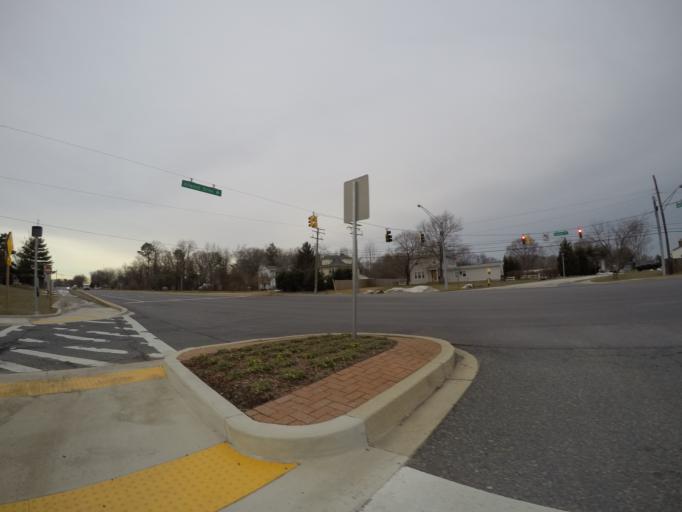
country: US
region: Maryland
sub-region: Anne Arundel County
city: Ferndale
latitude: 39.1798
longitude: -76.6510
